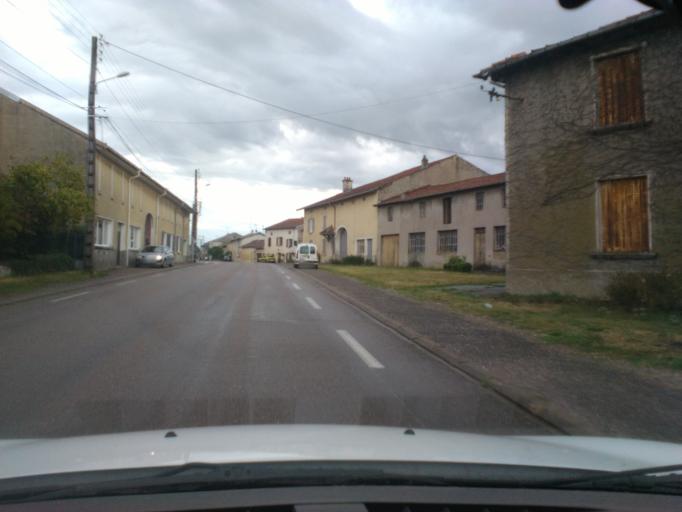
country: FR
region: Lorraine
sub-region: Departement de Meurthe-et-Moselle
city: Vezelise
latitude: 48.4214
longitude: 6.1293
